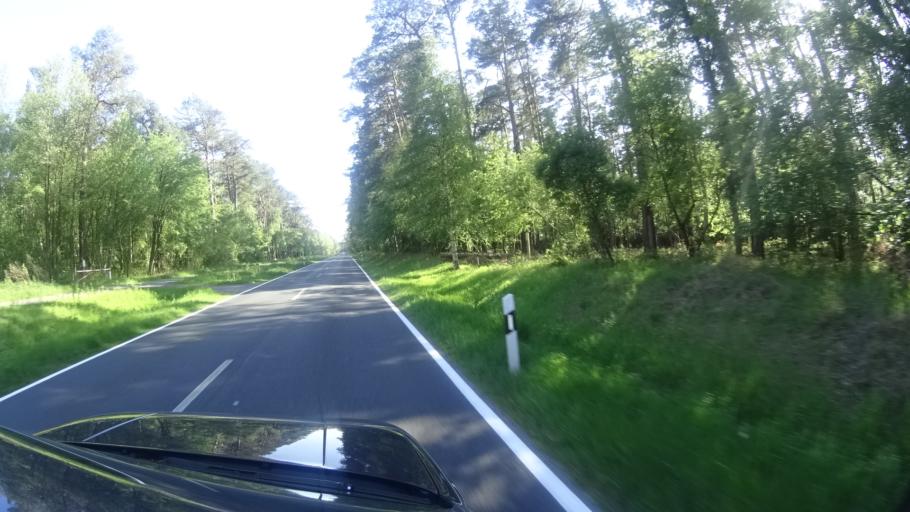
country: DE
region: Mecklenburg-Vorpommern
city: Ostseebad Prerow
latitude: 54.4315
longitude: 12.5747
